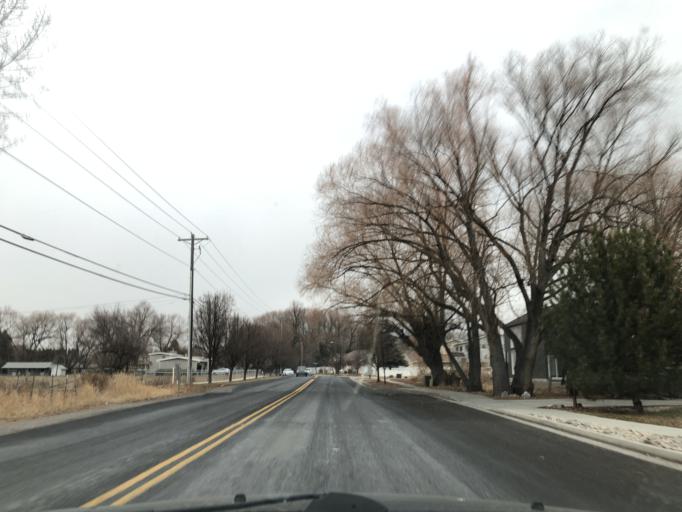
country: US
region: Utah
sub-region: Cache County
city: Logan
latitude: 41.7170
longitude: -111.8528
